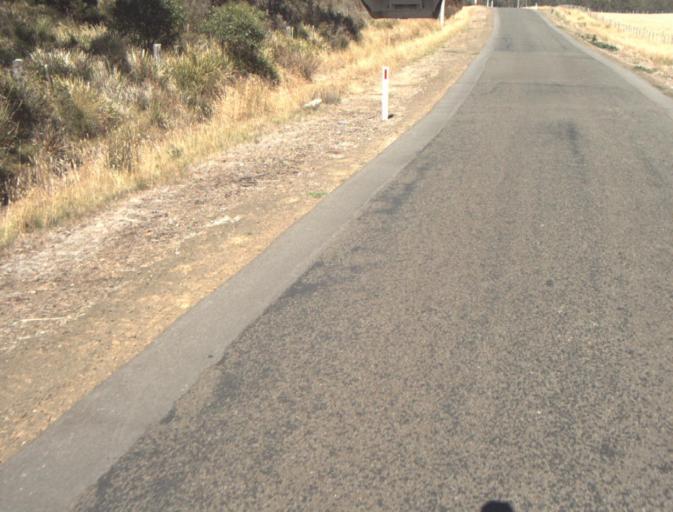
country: AU
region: Tasmania
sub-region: Launceston
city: Newstead
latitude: -41.3281
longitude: 147.3119
